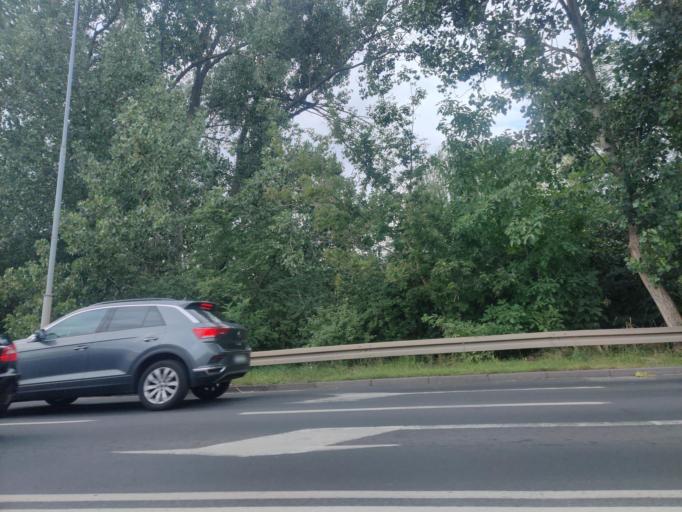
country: PL
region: Greater Poland Voivodeship
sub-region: Konin
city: Konin
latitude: 52.2235
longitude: 18.2523
